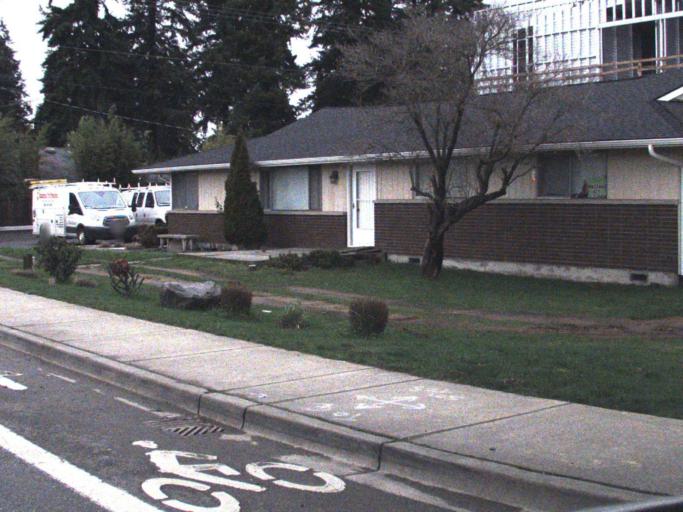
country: US
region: Washington
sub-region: Snohomish County
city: Smokey Point
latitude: 48.1524
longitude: -122.1738
